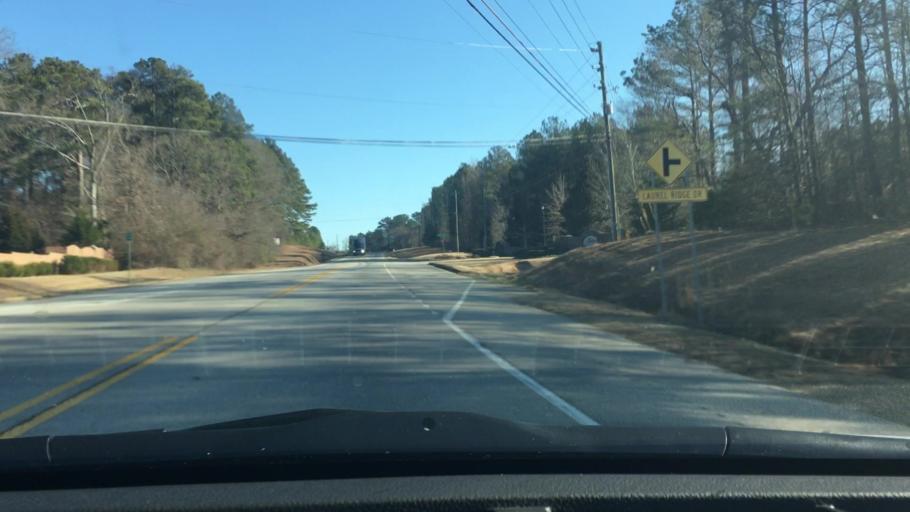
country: US
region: Georgia
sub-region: Henry County
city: McDonough
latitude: 33.4873
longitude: -84.0906
